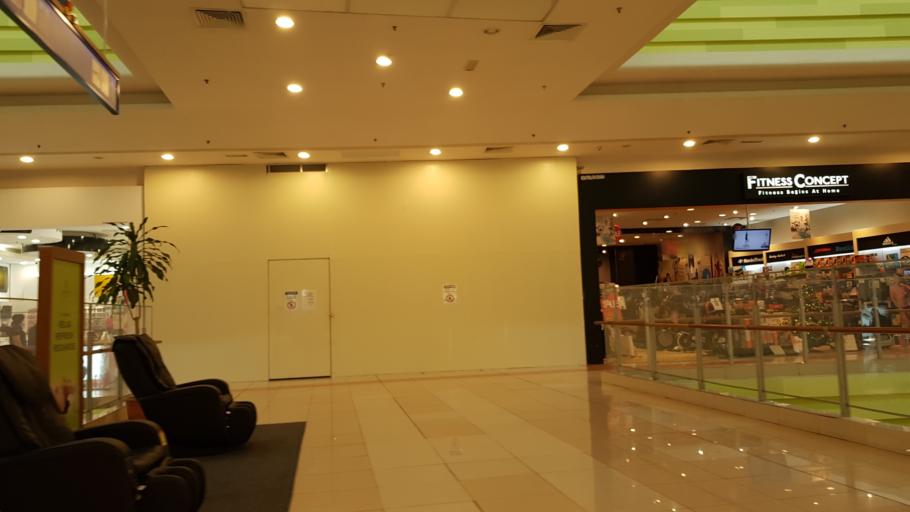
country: MY
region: Selangor
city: Klang
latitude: 2.9934
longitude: 101.4447
